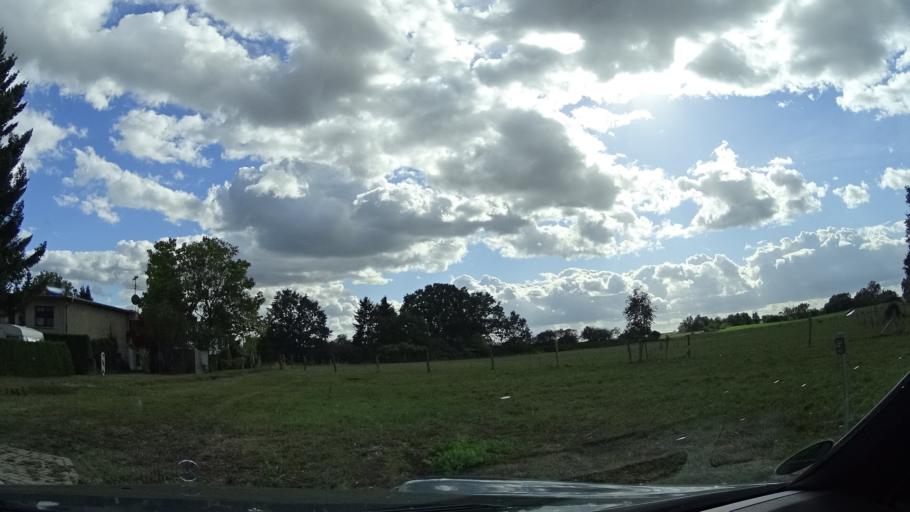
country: DE
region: Brandenburg
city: Neuruppin
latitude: 52.8899
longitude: 12.7965
